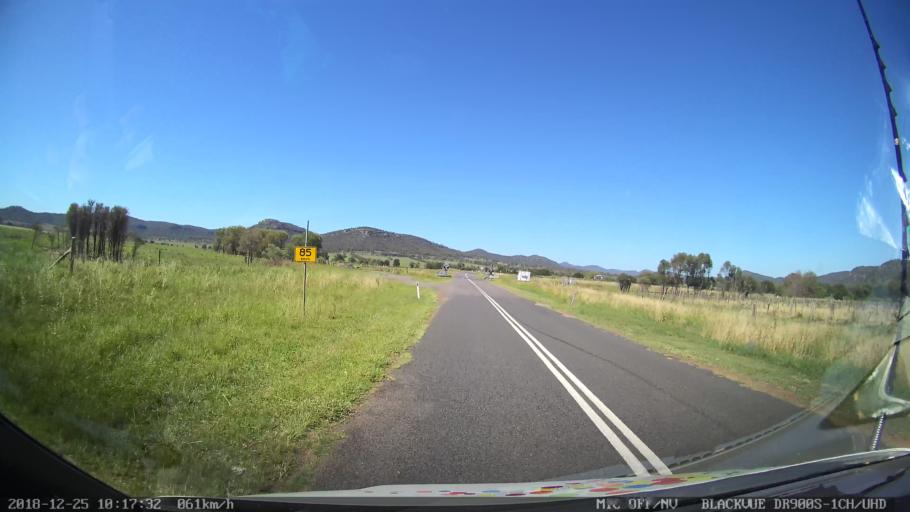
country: AU
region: New South Wales
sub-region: Muswellbrook
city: Denman
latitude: -32.3431
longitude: 150.5777
